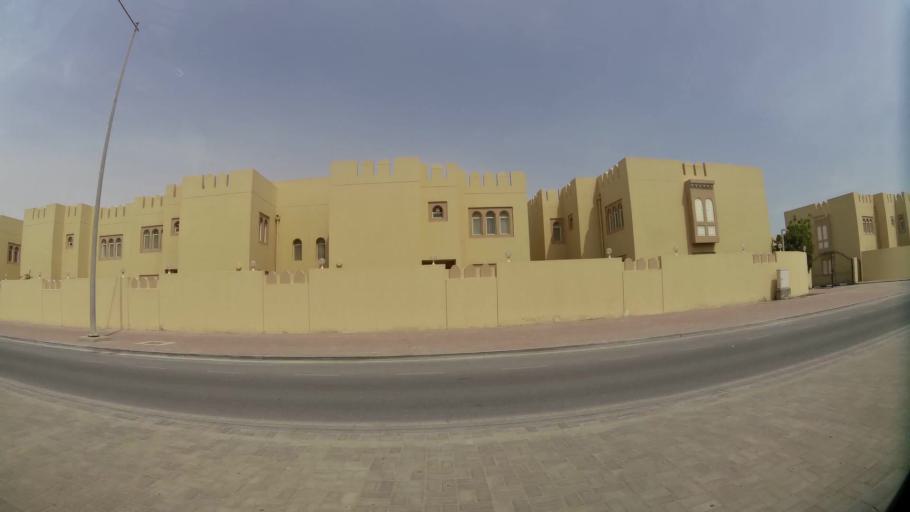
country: QA
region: Baladiyat ad Dawhah
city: Doha
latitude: 25.2685
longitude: 51.4836
